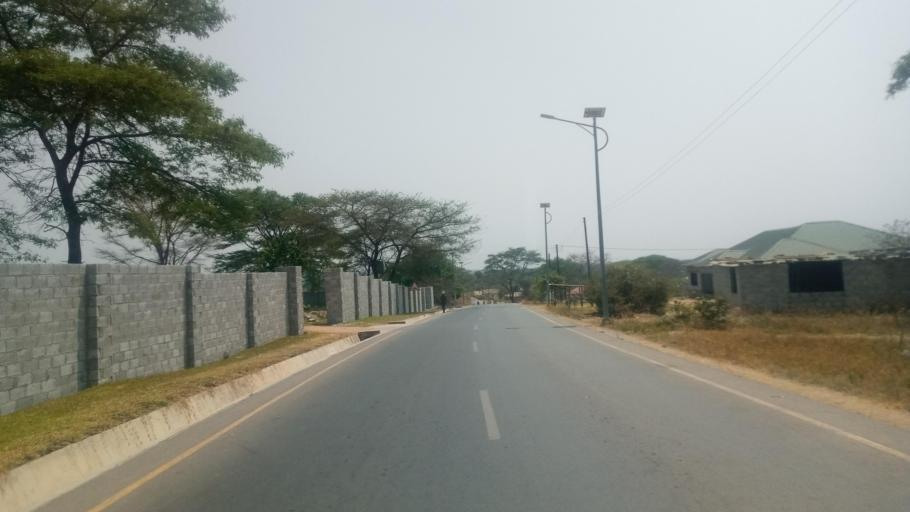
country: ZM
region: Lusaka
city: Lusaka
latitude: -15.4525
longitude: 28.4409
